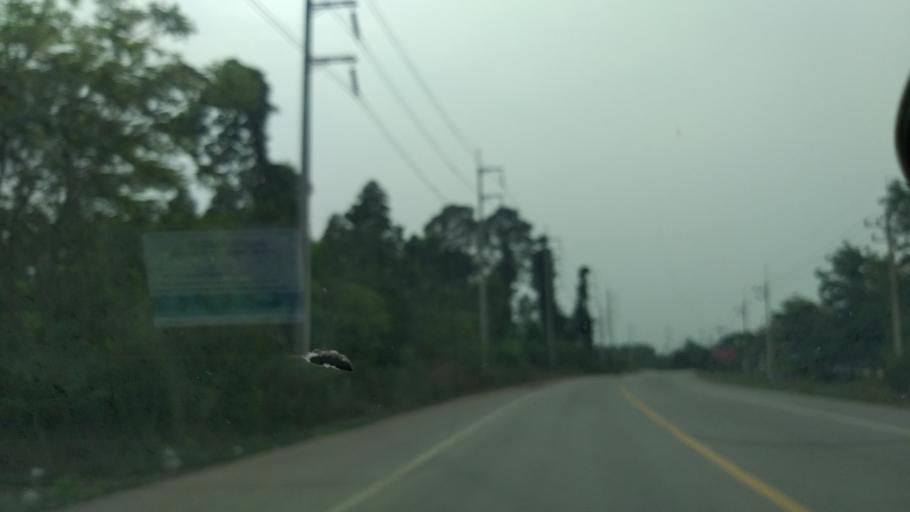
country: TH
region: Chachoengsao
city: Plaeng Yao
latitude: 13.5703
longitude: 101.2652
